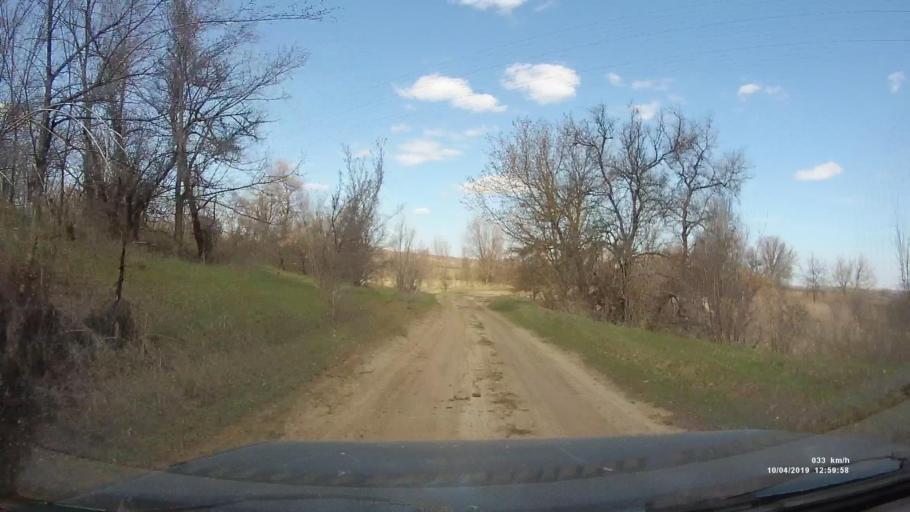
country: RU
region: Rostov
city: Masalovka
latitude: 48.3796
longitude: 40.2293
